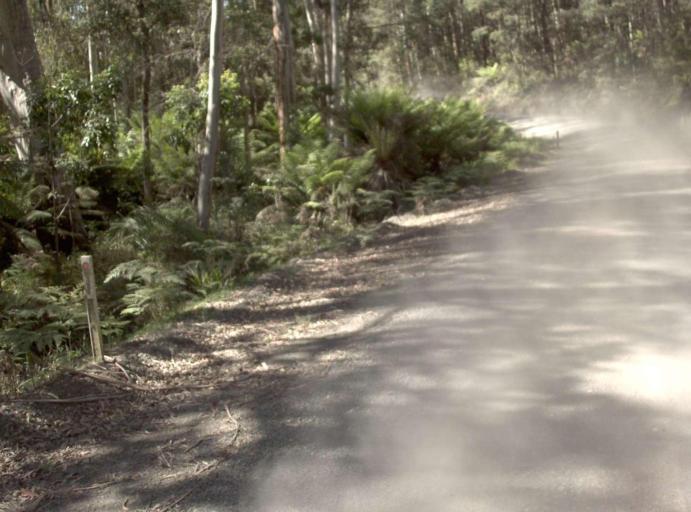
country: AU
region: New South Wales
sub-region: Bombala
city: Bombala
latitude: -37.2174
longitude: 148.7464
